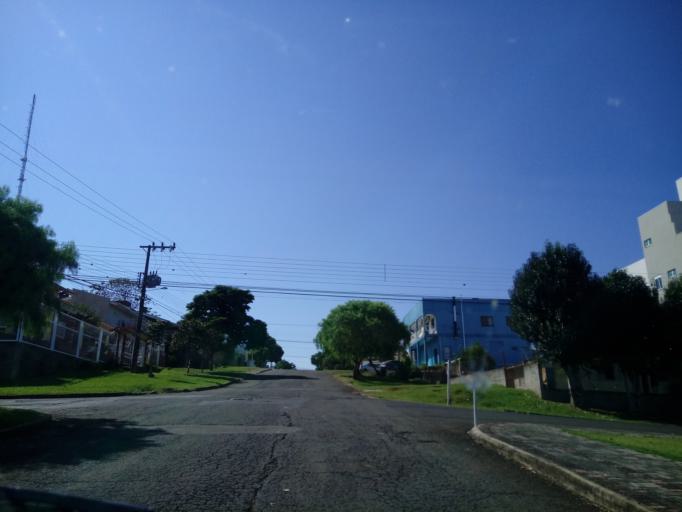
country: BR
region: Santa Catarina
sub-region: Chapeco
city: Chapeco
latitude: -27.0929
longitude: -52.5997
